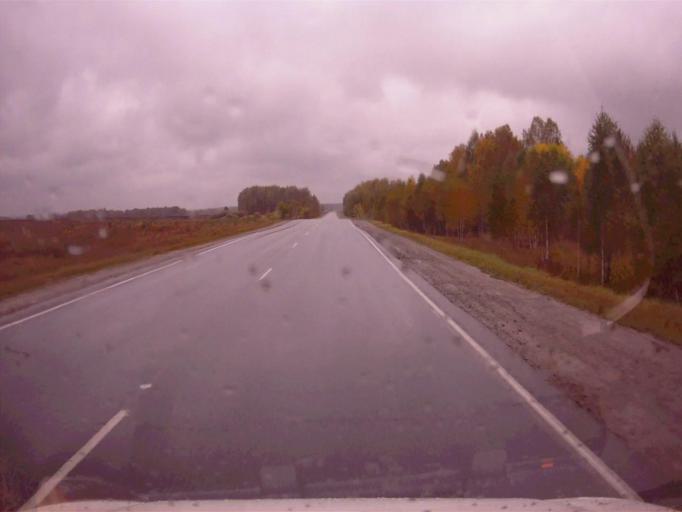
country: RU
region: Chelyabinsk
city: Argayash
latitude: 55.4785
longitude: 60.8328
